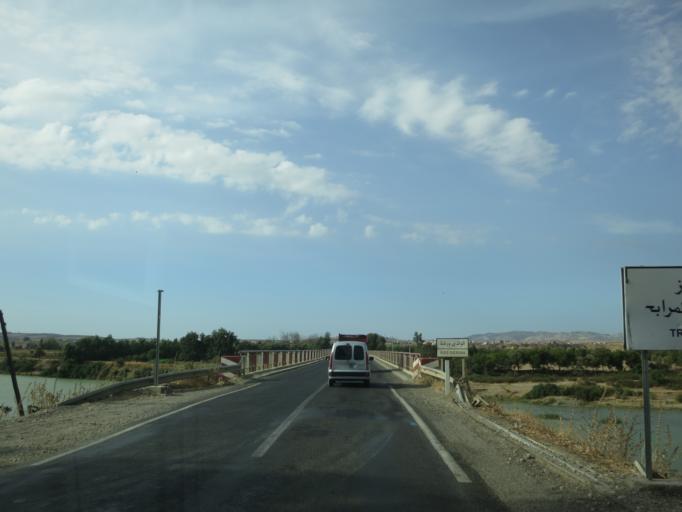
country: MA
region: Gharb-Chrarda-Beni Hssen
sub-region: Sidi-Kacem
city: Sidi Bousber
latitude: 34.4633
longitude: -5.5078
